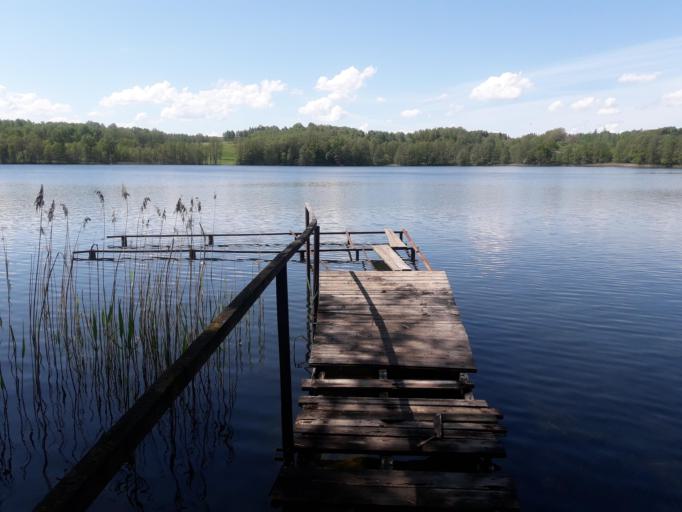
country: LT
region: Alytaus apskritis
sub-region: Alytaus rajonas
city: Daugai
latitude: 54.3839
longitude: 24.2912
